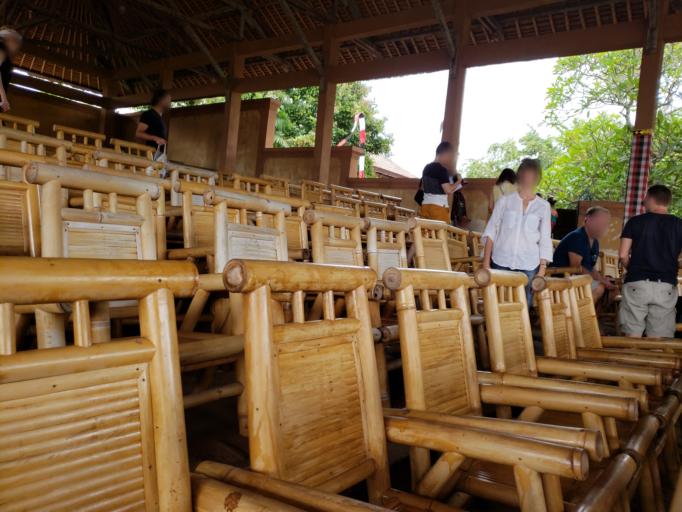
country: ID
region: Bali
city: Banjar Jabejero
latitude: -8.6061
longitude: 115.2559
